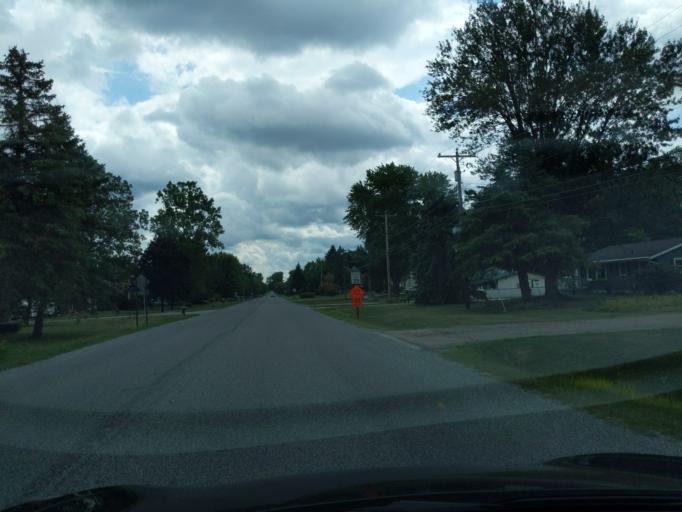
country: US
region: Michigan
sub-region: Eaton County
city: Dimondale
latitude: 42.6615
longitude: -84.5826
